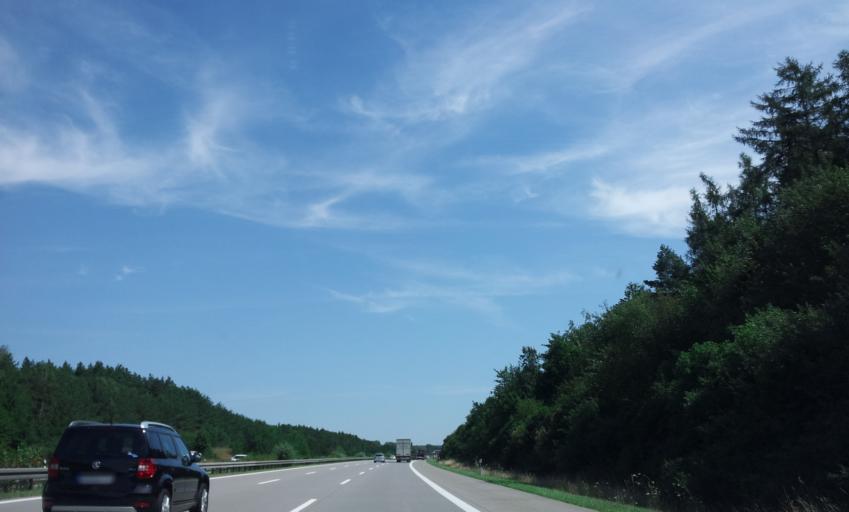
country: DE
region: Brandenburg
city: Erkner
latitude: 52.3703
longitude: 13.7666
